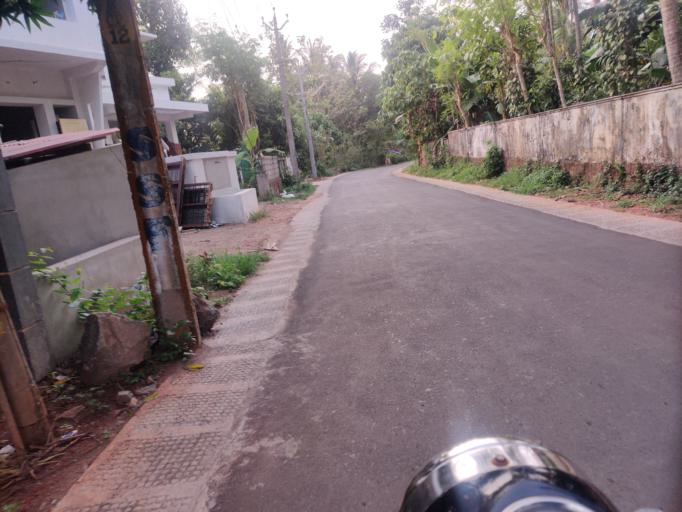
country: IN
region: Kerala
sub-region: Kozhikode
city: Mavoor
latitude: 11.2632
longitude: 75.9501
